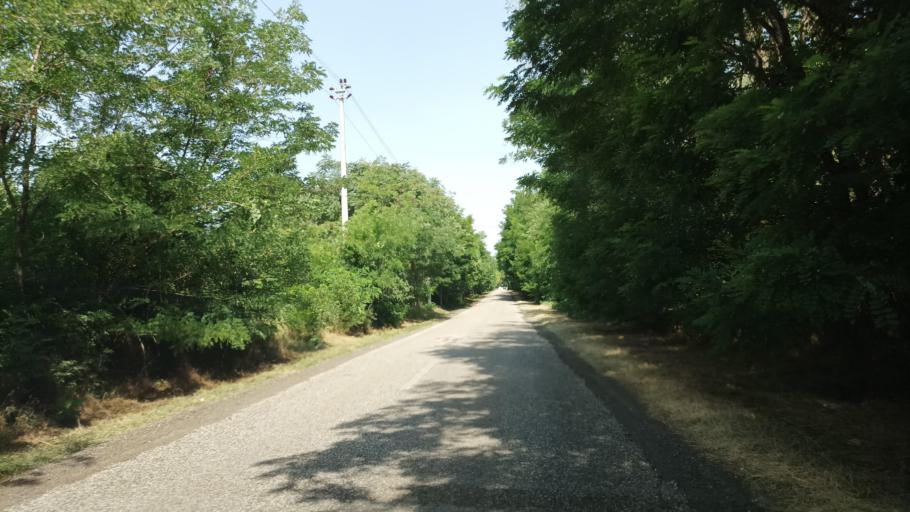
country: HU
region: Pest
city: Szigetujfalu
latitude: 47.2013
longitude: 18.9175
